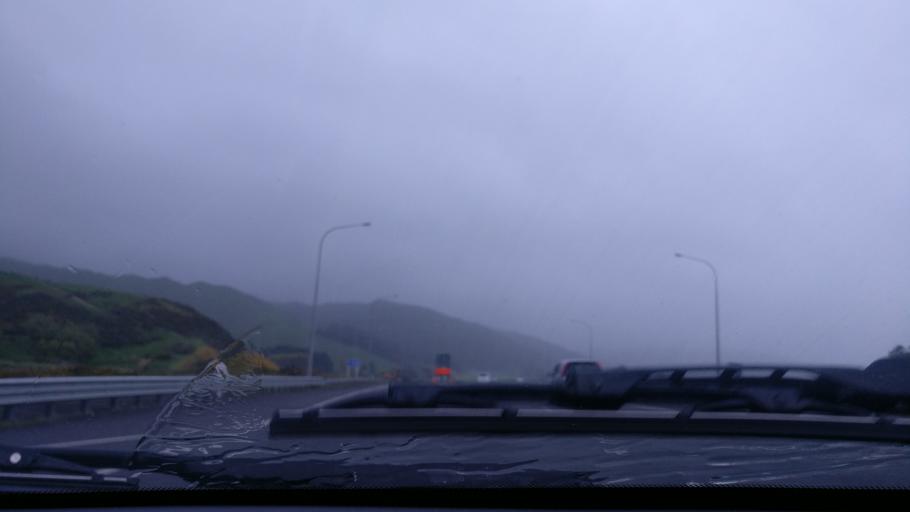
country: NZ
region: Wellington
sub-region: Kapiti Coast District
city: Paraparaumu
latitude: -40.9681
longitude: 174.9847
